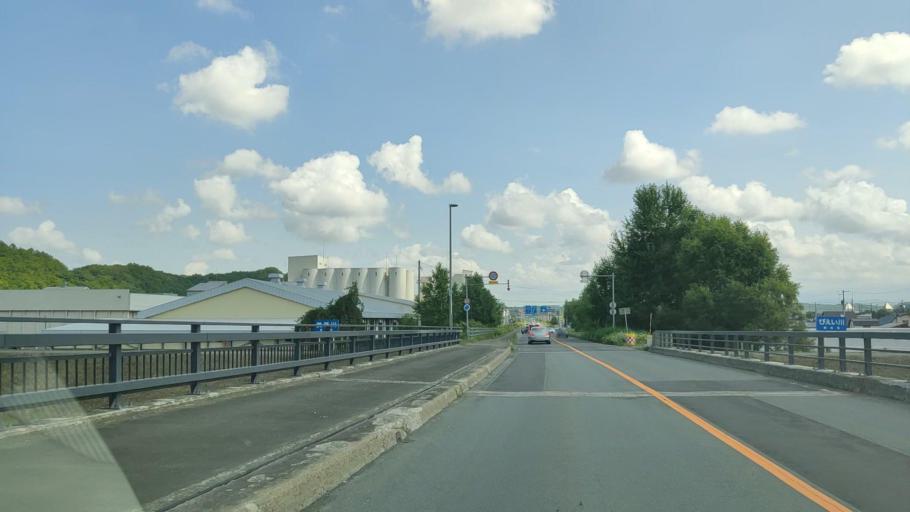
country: JP
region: Hokkaido
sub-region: Asahikawa-shi
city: Asahikawa
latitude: 43.5889
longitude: 142.4511
